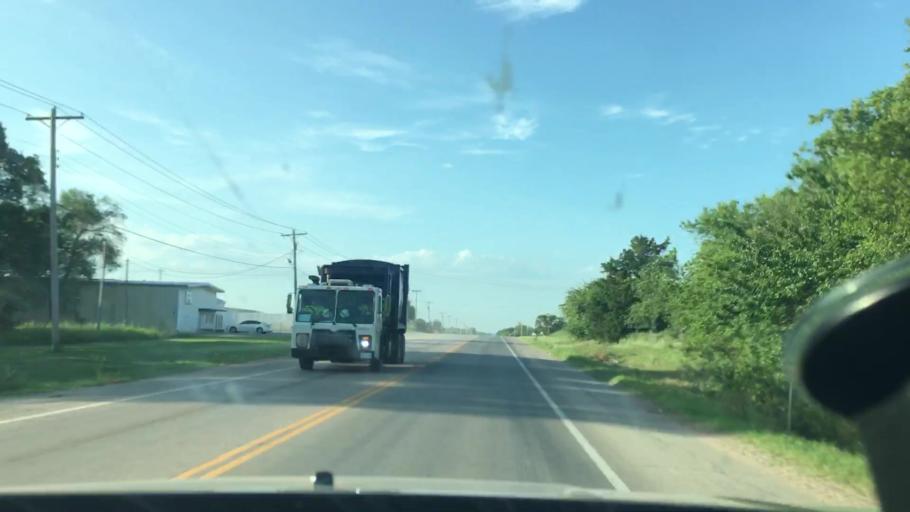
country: US
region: Oklahoma
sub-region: Garvin County
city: Pauls Valley
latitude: 34.7113
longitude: -97.2129
